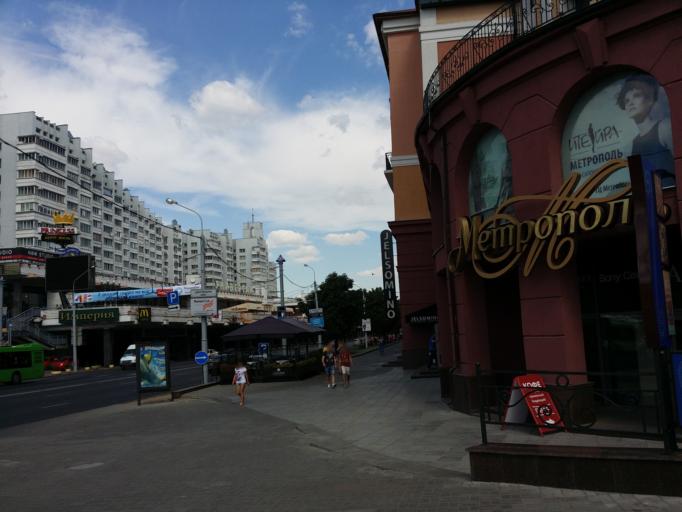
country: BY
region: Minsk
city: Minsk
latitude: 53.9018
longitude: 27.5490
